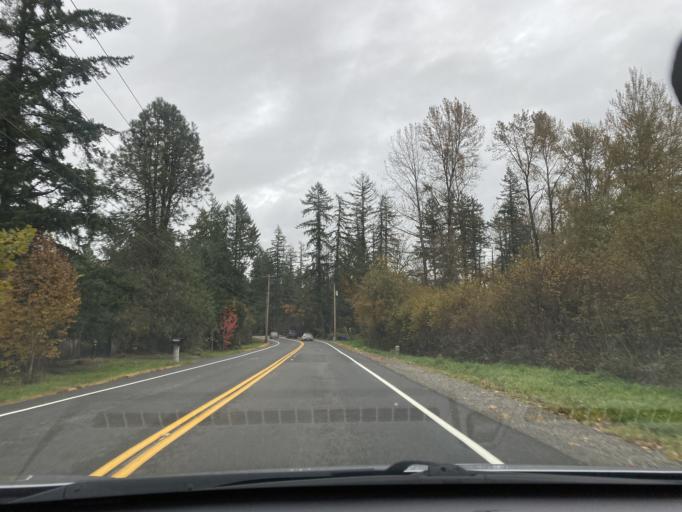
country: US
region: Washington
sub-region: King County
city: Lake Morton-Berrydale
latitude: 47.3021
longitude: -122.1145
